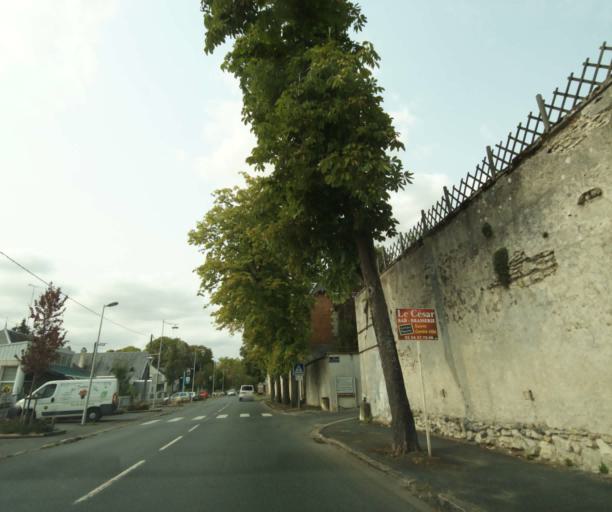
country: FR
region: Centre
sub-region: Departement de l'Indre
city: Chatillon-sur-Indre
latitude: 46.9866
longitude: 1.1725
